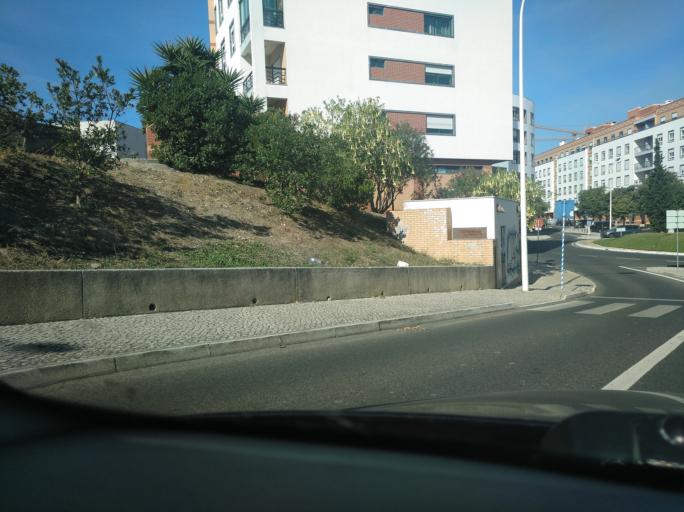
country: PT
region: Lisbon
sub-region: Oeiras
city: Alges
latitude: 38.7072
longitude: -9.2329
